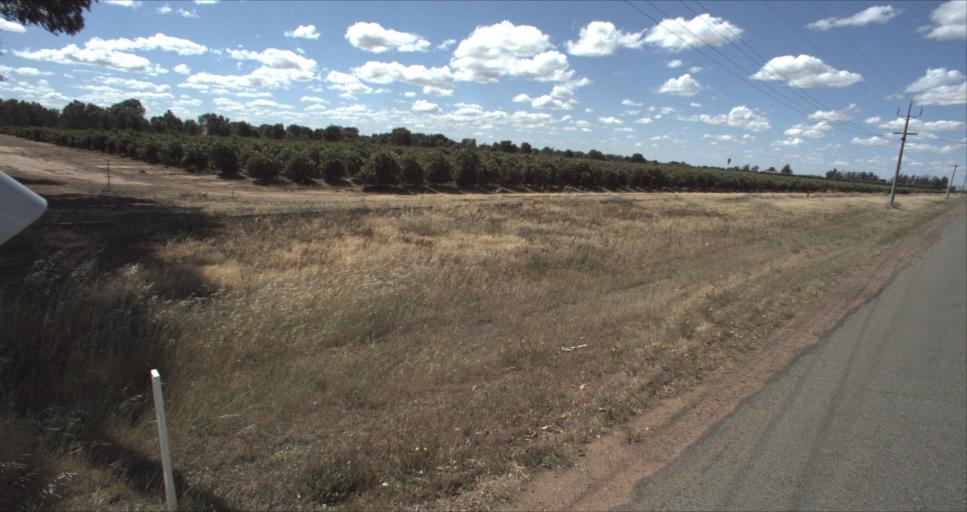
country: AU
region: New South Wales
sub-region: Leeton
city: Leeton
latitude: -34.5167
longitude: 146.2365
